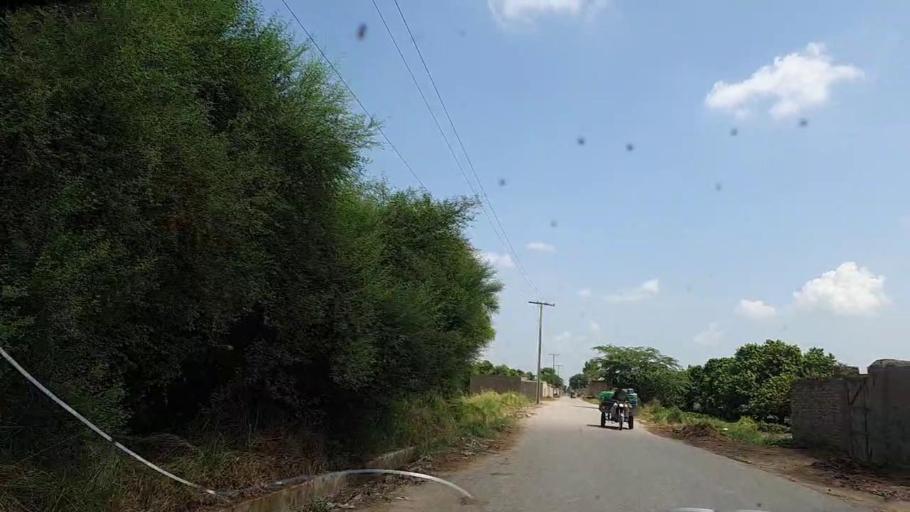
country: PK
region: Sindh
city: Tharu Shah
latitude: 26.9619
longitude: 68.0988
